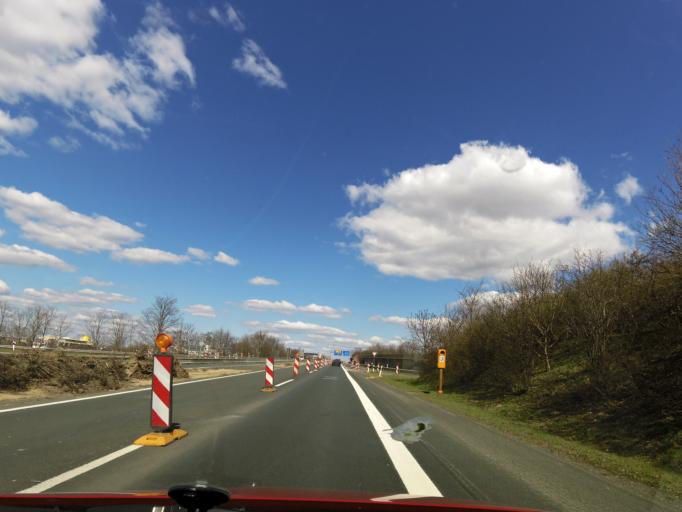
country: DE
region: Lower Saxony
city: Braunschweig
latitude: 52.3061
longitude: 10.5104
